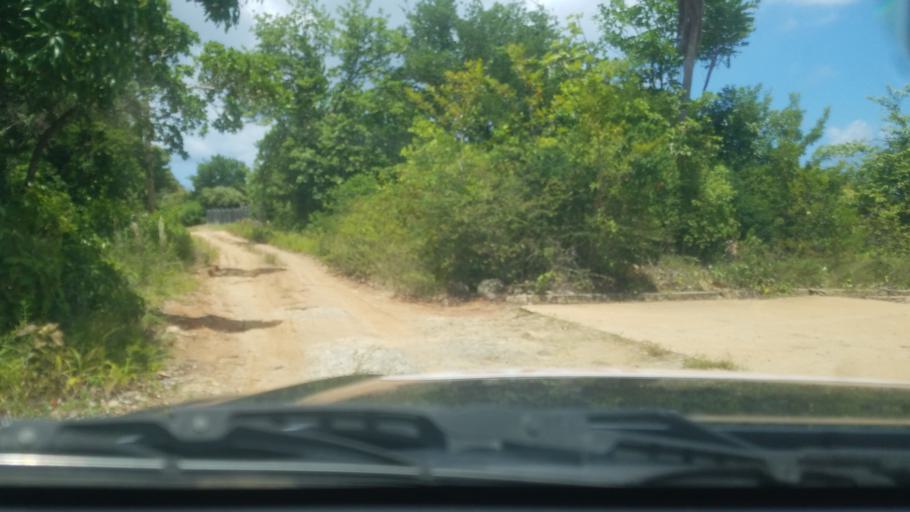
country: LC
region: Dennery Quarter
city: Dennery
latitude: 13.9206
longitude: -60.9029
